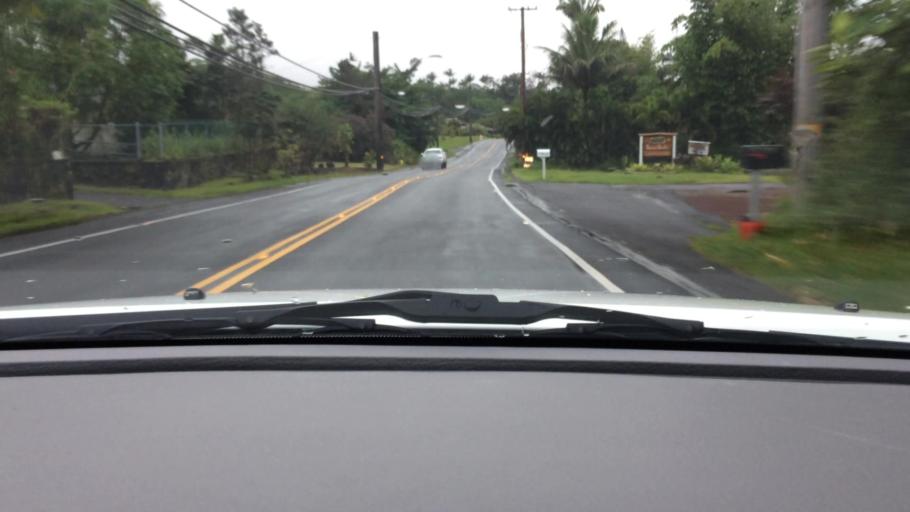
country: US
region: Hawaii
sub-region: Hawaii County
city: Hawaiian Paradise Park
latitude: 19.4962
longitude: -154.9504
